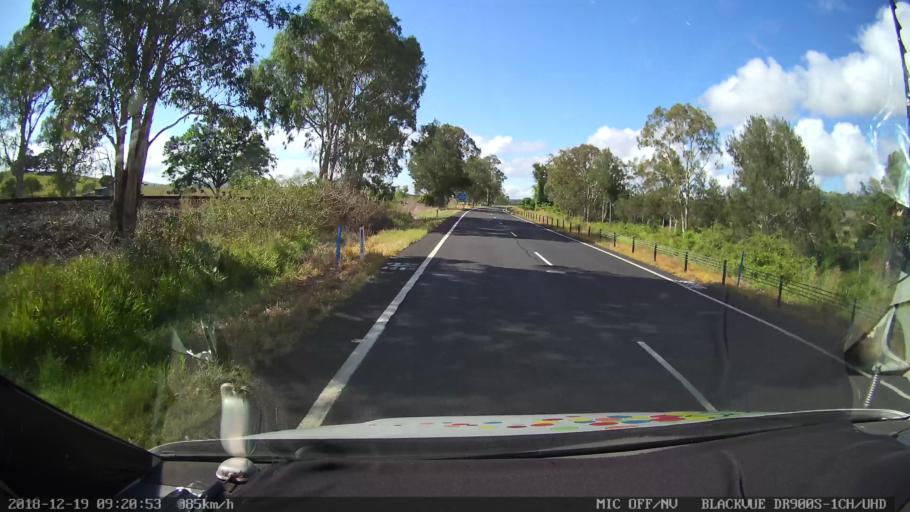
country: AU
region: New South Wales
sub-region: Kyogle
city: Kyogle
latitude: -28.5768
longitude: 152.9826
